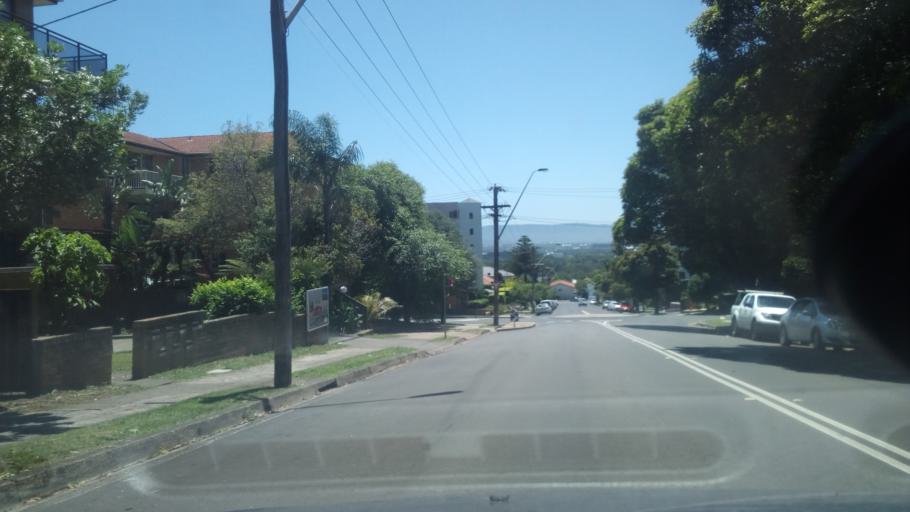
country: AU
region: New South Wales
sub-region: Wollongong
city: Wollongong
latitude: -34.4168
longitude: 150.8972
